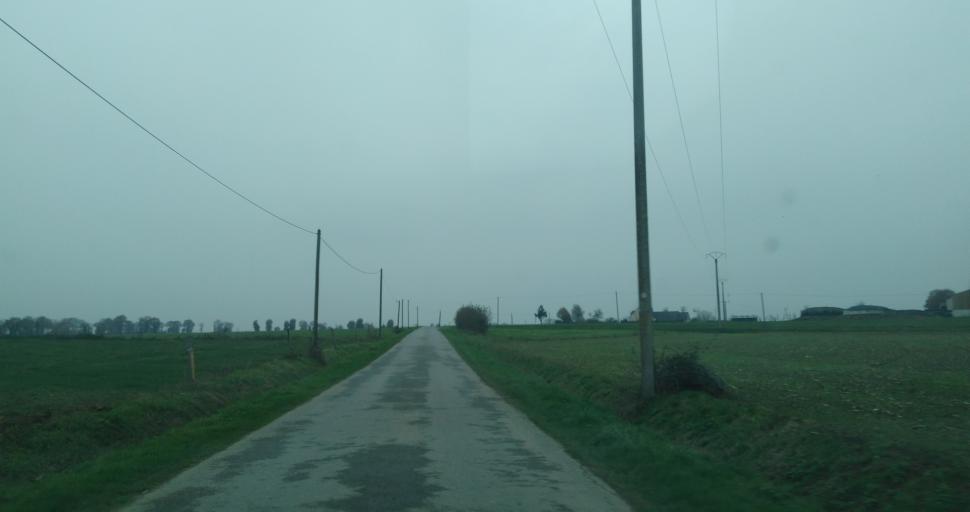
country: FR
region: Brittany
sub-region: Departement d'Ille-et-Vilaine
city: Iffendic
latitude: 48.0952
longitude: -2.0819
